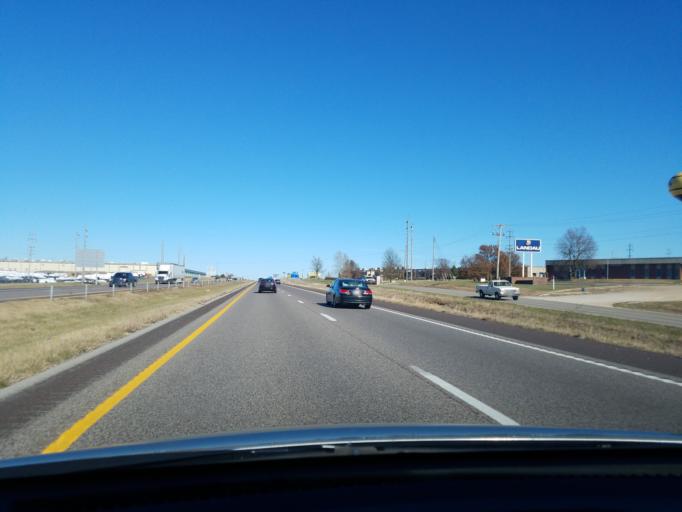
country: US
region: Missouri
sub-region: Laclede County
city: Lebanon
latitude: 37.6591
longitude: -92.6589
